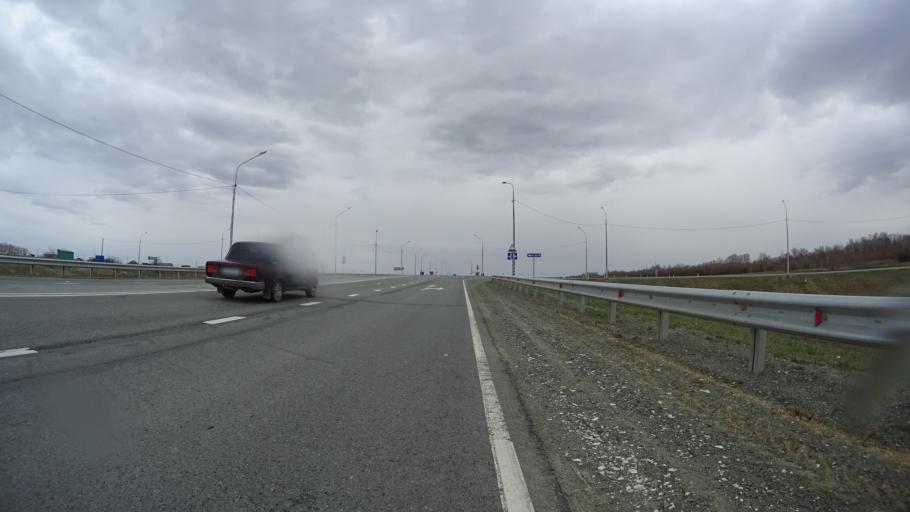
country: RU
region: Chelyabinsk
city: Krasnogorskiy
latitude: 54.6744
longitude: 61.2489
